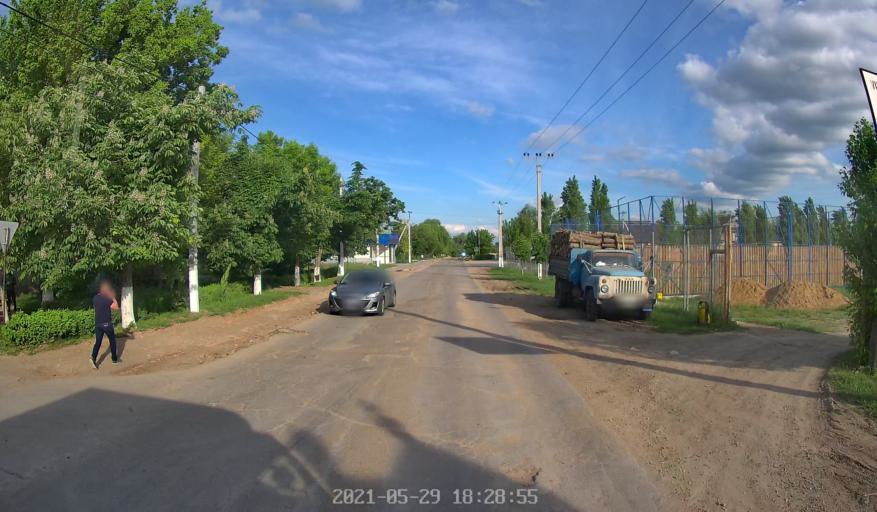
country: MD
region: Chisinau
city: Singera
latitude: 46.8273
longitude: 28.8696
